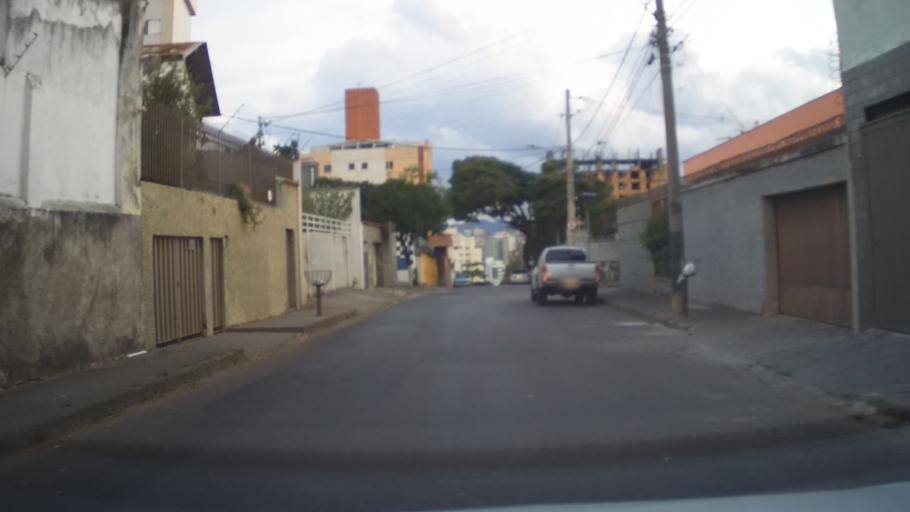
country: BR
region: Minas Gerais
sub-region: Belo Horizonte
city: Belo Horizonte
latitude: -19.9007
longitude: -43.9291
